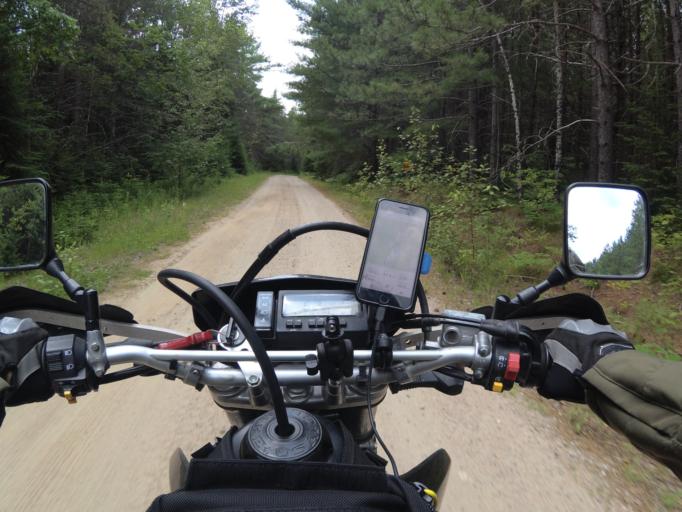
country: CA
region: Ontario
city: Bancroft
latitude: 45.0195
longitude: -77.2648
